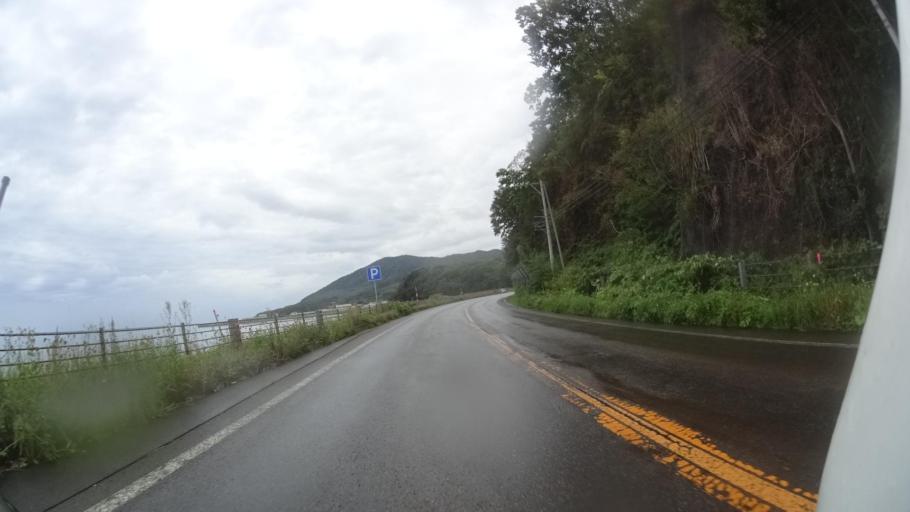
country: JP
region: Hokkaido
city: Kitami
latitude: 44.0959
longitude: 143.7956
